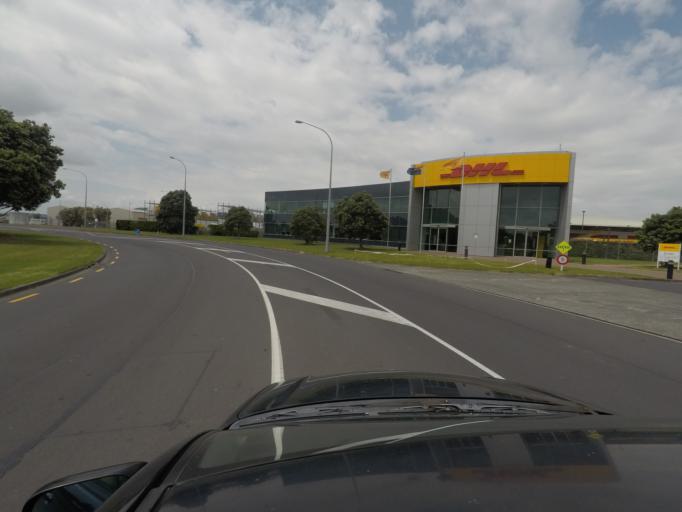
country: NZ
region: Auckland
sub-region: Auckland
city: Mangere
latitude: -37.0022
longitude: 174.8011
